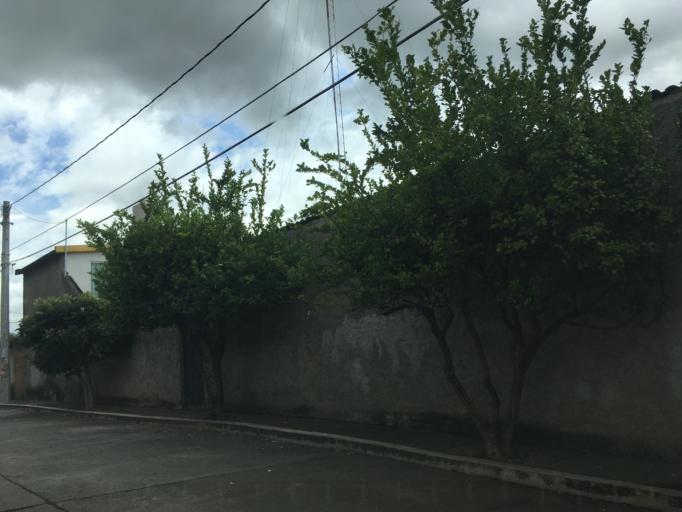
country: MX
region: Michoacan
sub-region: Morelia
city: Morelos
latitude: 19.6517
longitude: -101.2338
